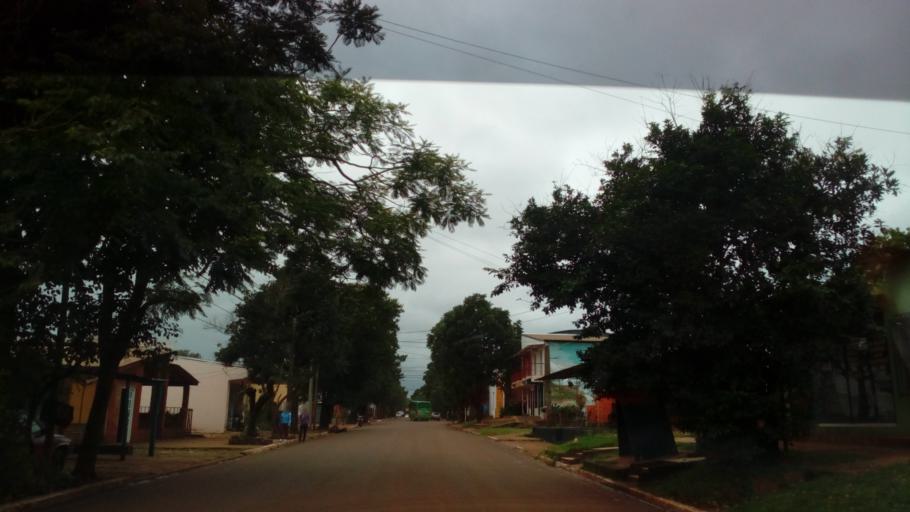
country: AR
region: Misiones
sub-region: Departamento de Candelaria
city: Candelaria
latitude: -27.4603
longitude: -55.7472
